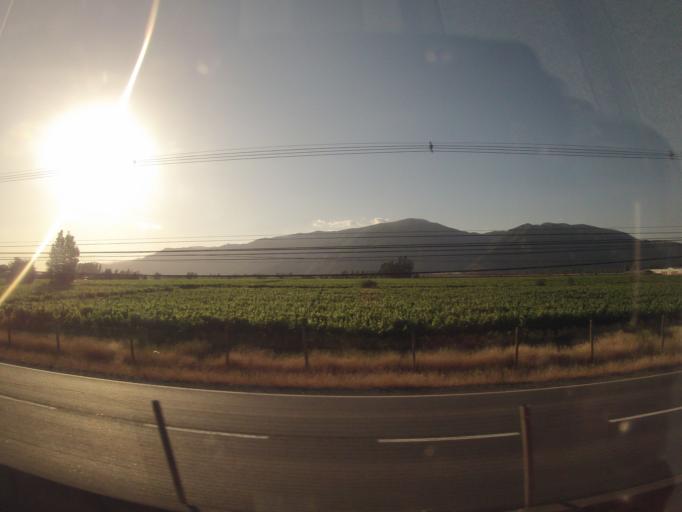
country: CL
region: O'Higgins
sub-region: Provincia de Cachapoal
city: San Vicente
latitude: -34.5575
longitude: -70.9651
